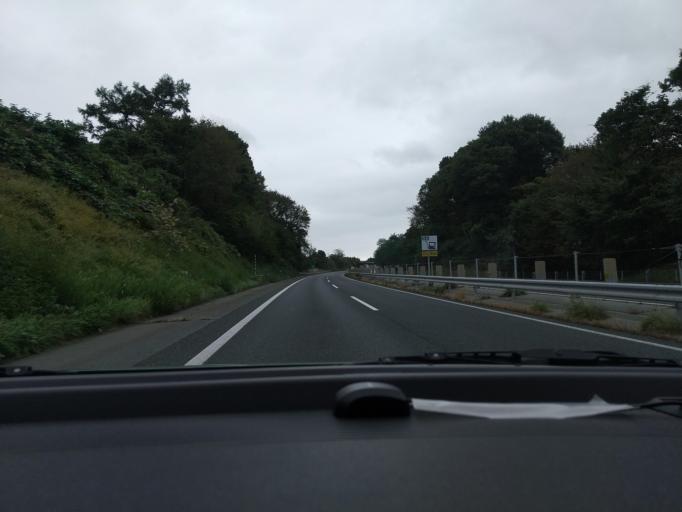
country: JP
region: Iwate
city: Mizusawa
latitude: 39.0519
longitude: 141.1073
